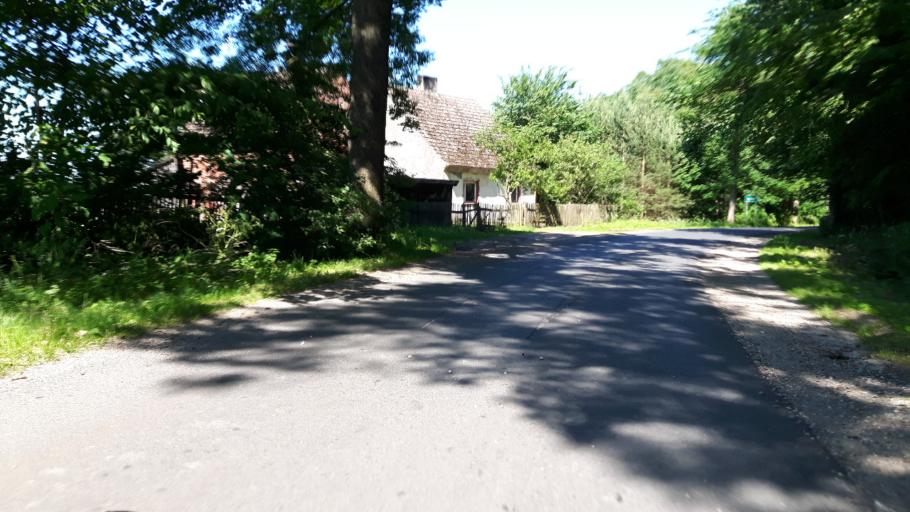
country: PL
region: Pomeranian Voivodeship
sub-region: Powiat slupski
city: Glowczyce
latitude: 54.6394
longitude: 17.4105
